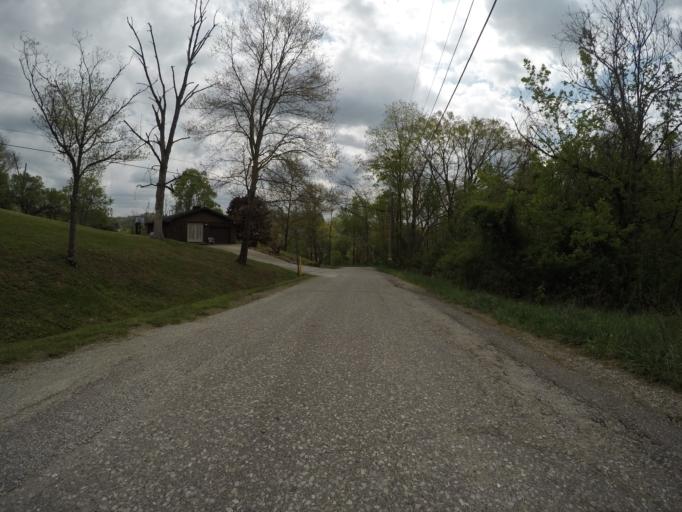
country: US
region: West Virginia
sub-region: Kanawha County
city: Charleston
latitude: 38.3914
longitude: -81.6037
